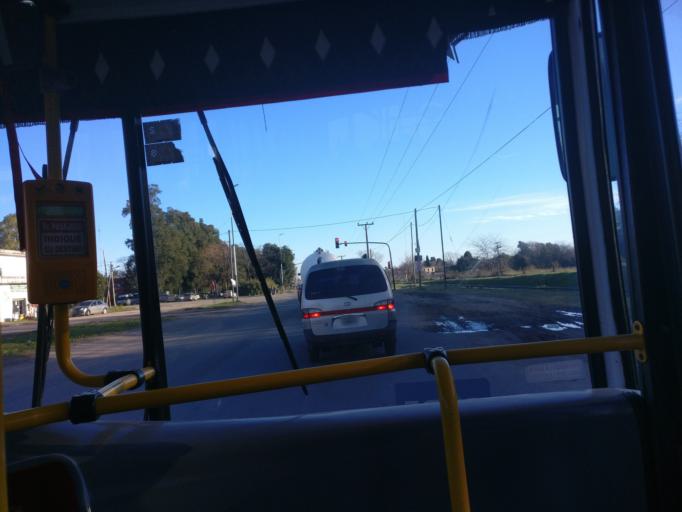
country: AR
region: Buenos Aires
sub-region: Partido de Ezeiza
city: Ezeiza
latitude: -34.9175
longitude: -58.6037
